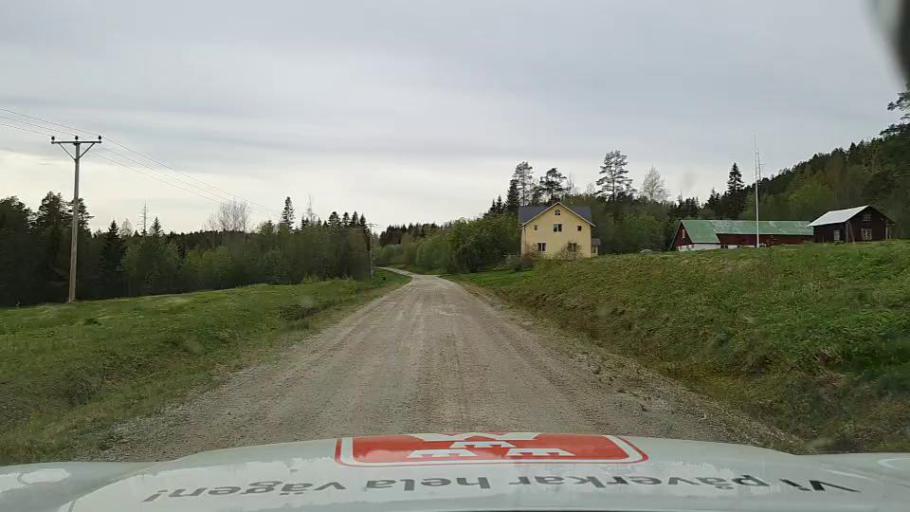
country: SE
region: Jaemtland
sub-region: Bergs Kommun
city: Hoverberg
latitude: 62.6672
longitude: 14.8174
